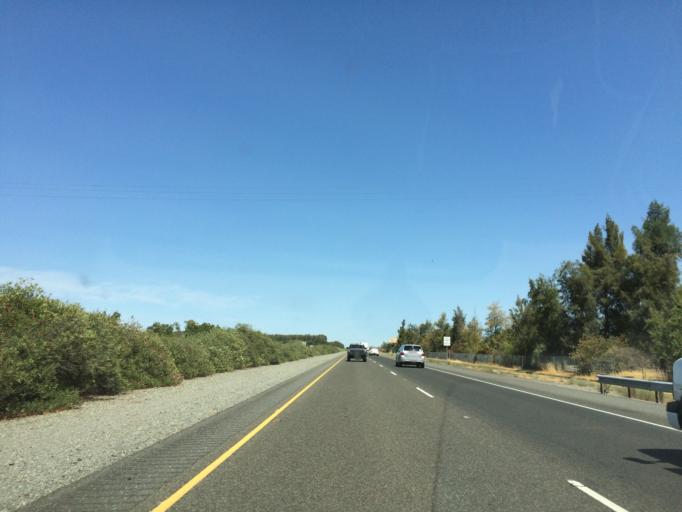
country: US
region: California
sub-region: Glenn County
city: Orland
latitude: 39.7541
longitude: -122.2054
